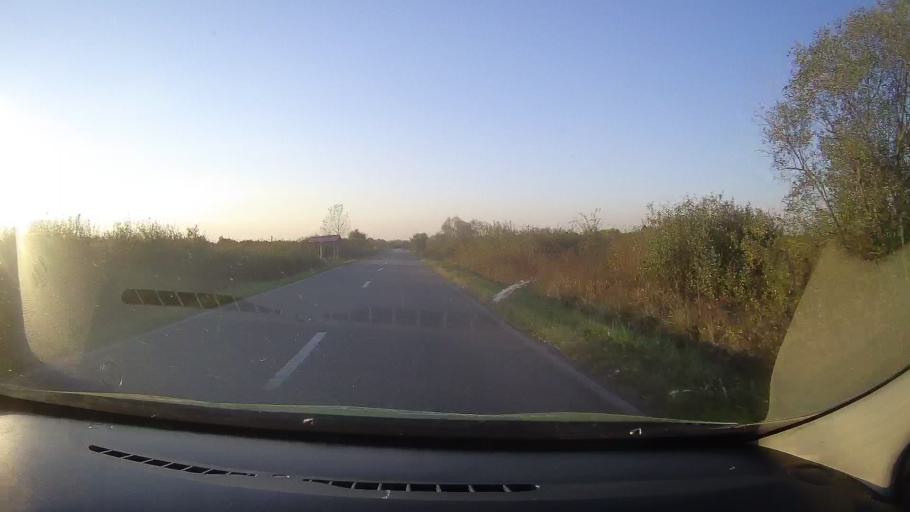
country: RO
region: Timis
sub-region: Comuna Traian Vuia
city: Traian Vuia
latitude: 45.7883
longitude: 22.0777
